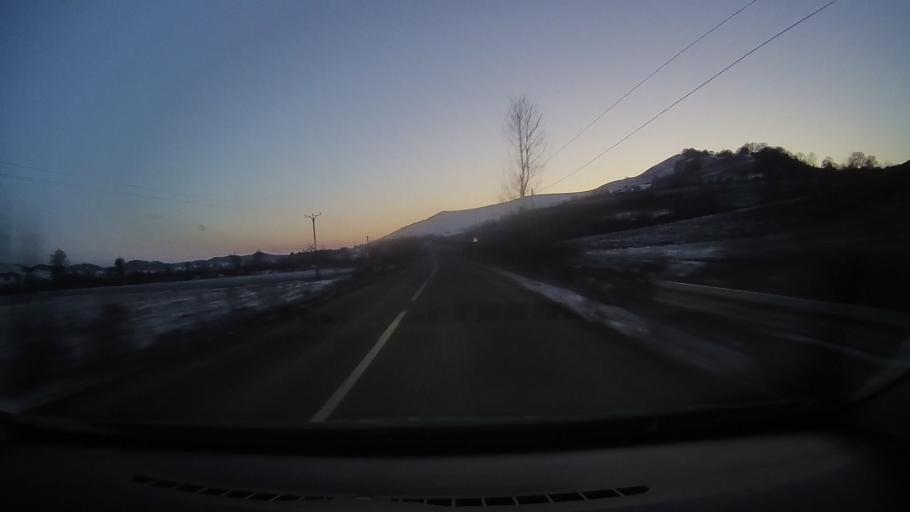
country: RO
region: Sibiu
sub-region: Comuna Alma
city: Alma
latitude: 46.2014
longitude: 24.4488
